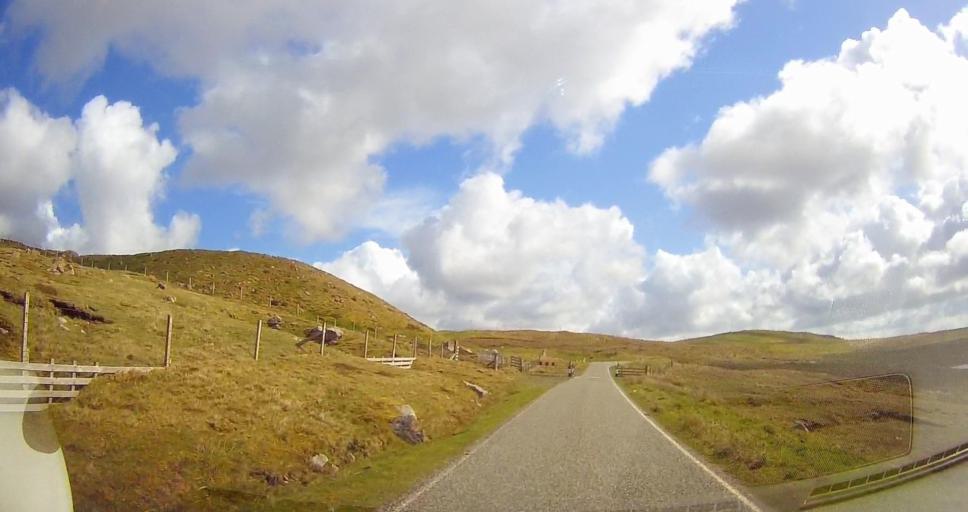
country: GB
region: Scotland
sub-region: Shetland Islands
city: Lerwick
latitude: 60.4912
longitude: -1.3902
